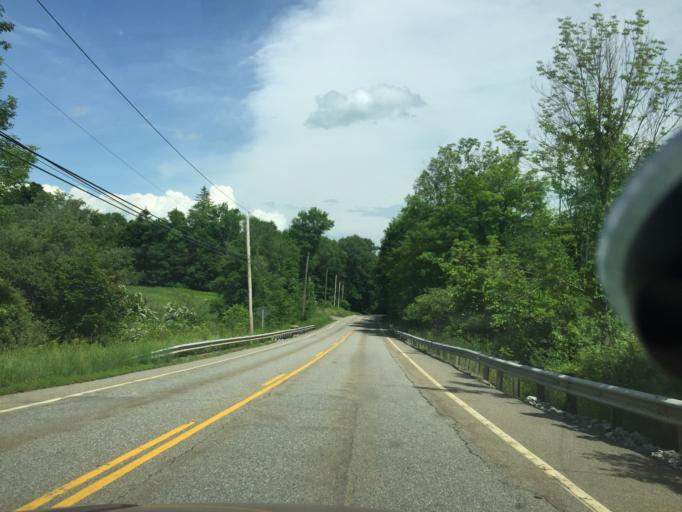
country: US
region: Connecticut
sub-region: Litchfield County
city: West Torrington
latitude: 41.8239
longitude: -73.1698
